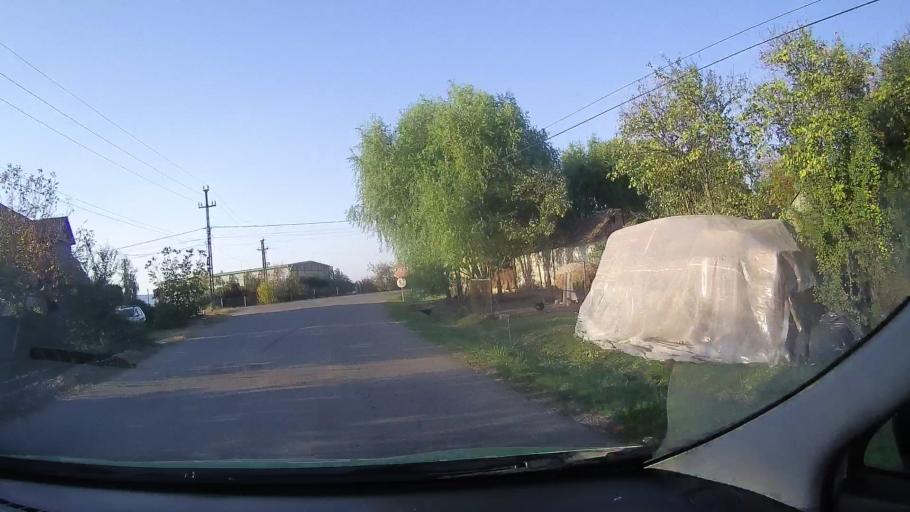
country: RO
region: Bihor
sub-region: Comuna Bors
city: Bors
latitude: 47.1145
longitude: 21.8225
